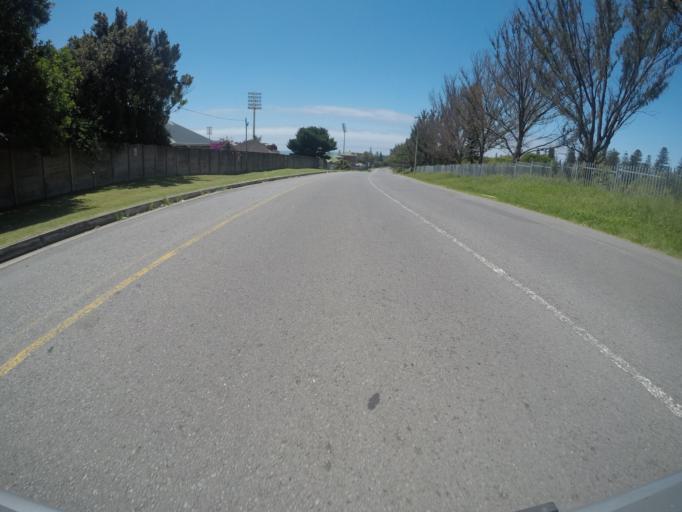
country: ZA
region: Eastern Cape
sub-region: Buffalo City Metropolitan Municipality
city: East London
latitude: -33.0074
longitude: 27.9169
